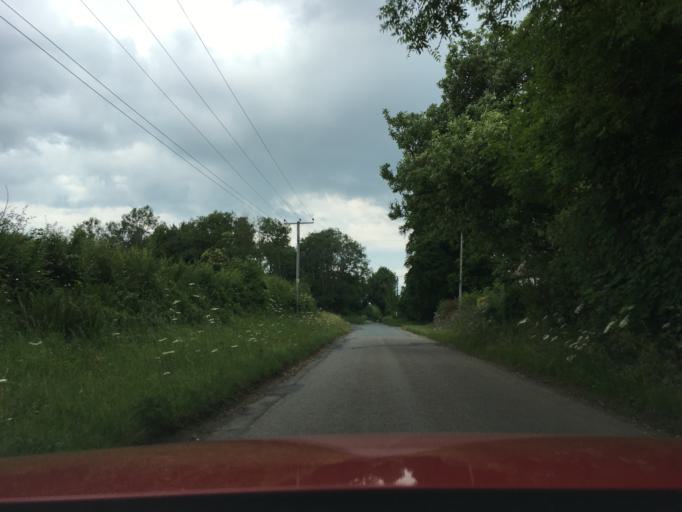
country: GB
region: England
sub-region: Gloucestershire
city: Coates
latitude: 51.7509
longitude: -2.0554
